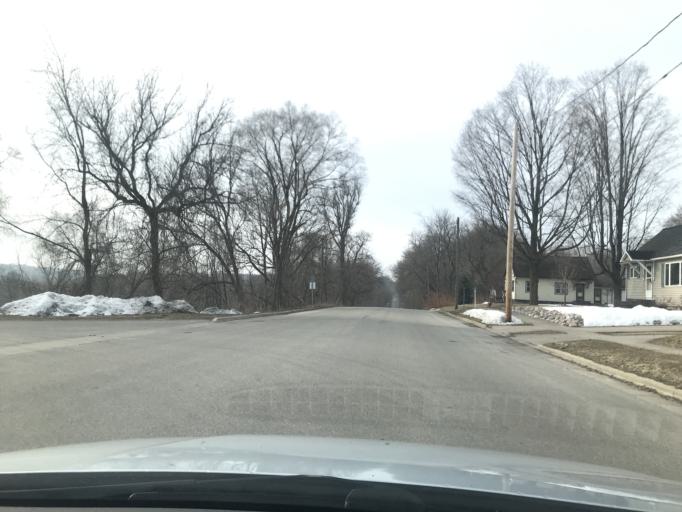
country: US
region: Wisconsin
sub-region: Oconto County
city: Oconto Falls
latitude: 44.8687
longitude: -88.1466
